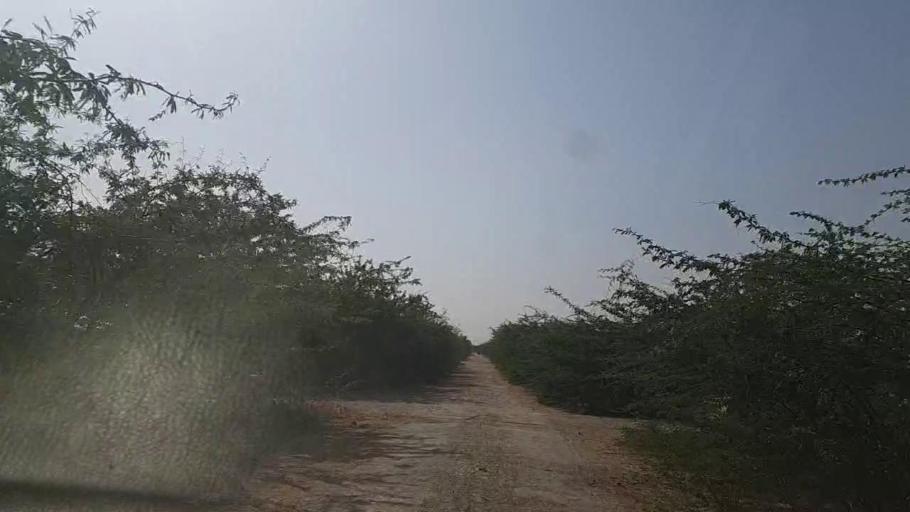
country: PK
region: Sindh
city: Kadhan
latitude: 24.5689
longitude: 69.2786
